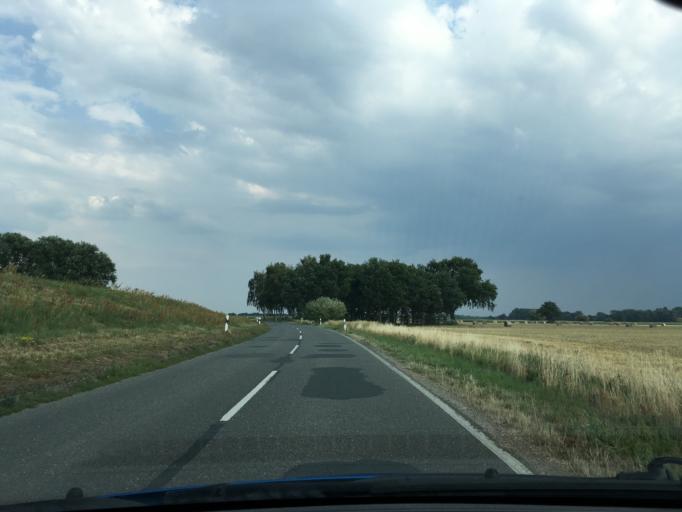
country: DE
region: Lower Saxony
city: Dannenberg
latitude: 53.1345
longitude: 11.0874
